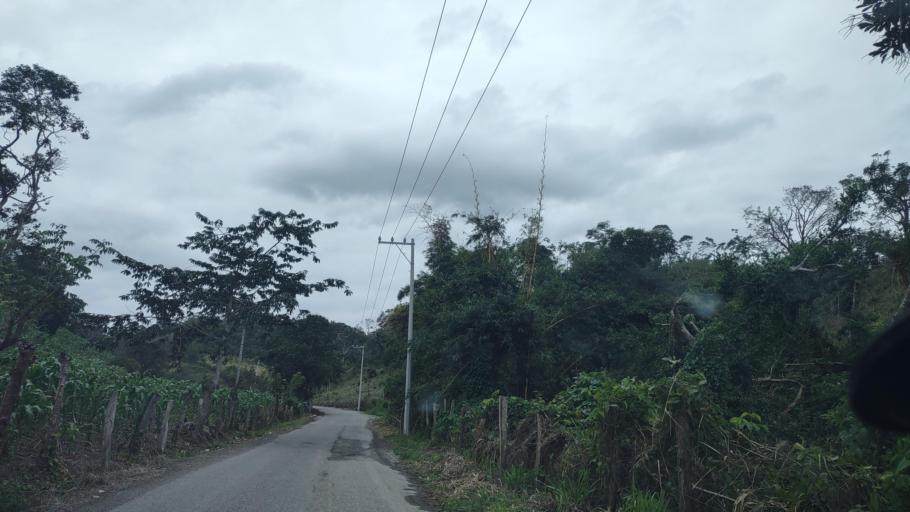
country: MX
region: Veracruz
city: Papantla de Olarte
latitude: 20.4442
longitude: -97.2978
